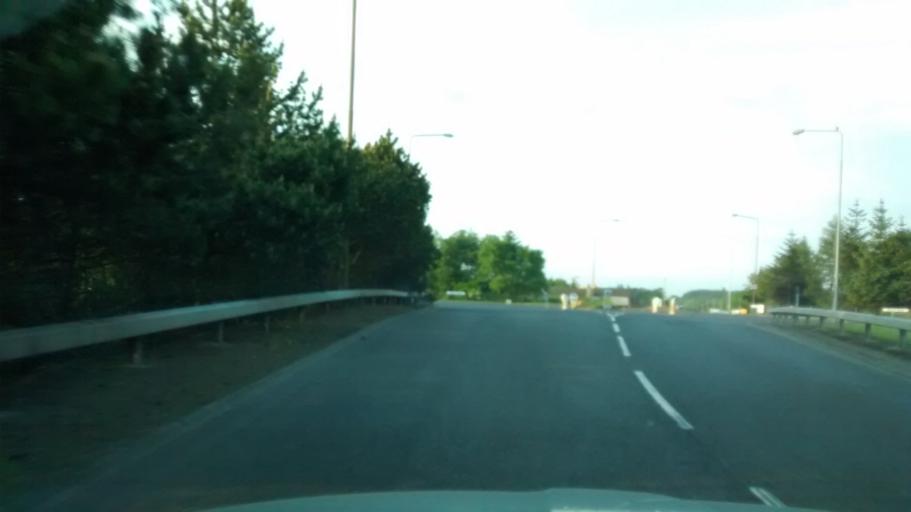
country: GB
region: Scotland
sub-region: West Lothian
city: West Calder
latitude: 55.9053
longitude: -3.5764
